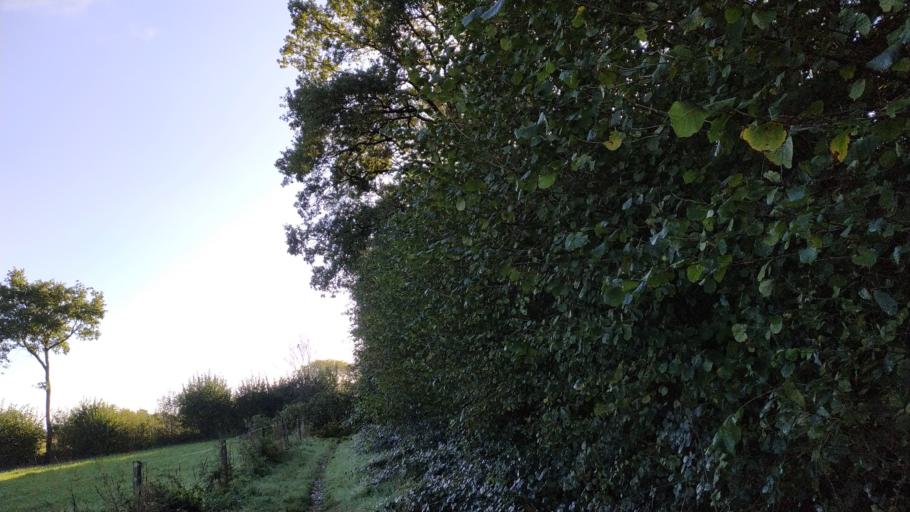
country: FR
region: Brittany
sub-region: Departement d'Ille-et-Vilaine
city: Chantepie
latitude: 48.0774
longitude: -1.6190
